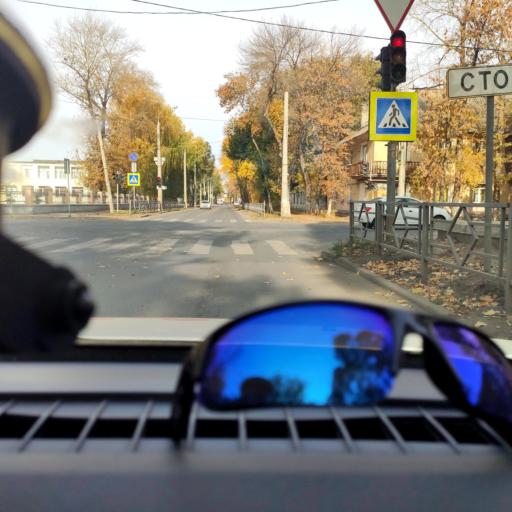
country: RU
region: Samara
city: Samara
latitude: 53.1133
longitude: 50.0733
